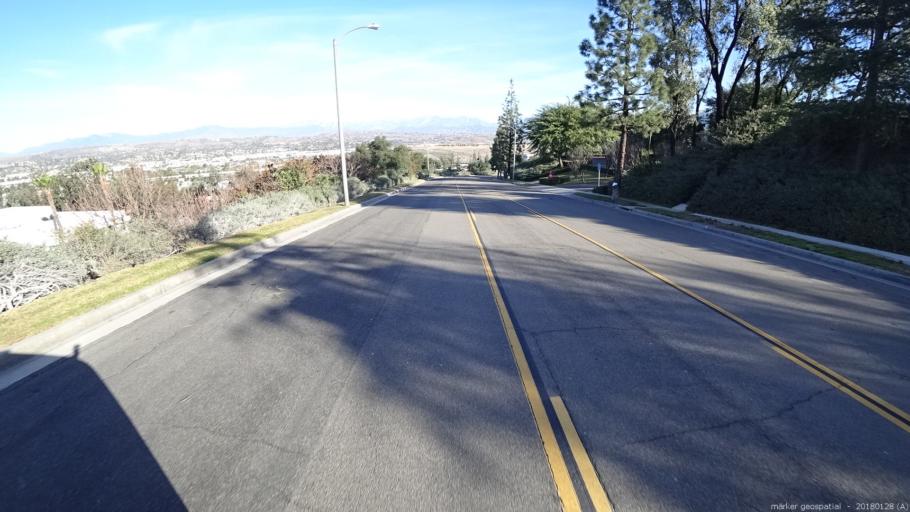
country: US
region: California
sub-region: Los Angeles County
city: Walnut
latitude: 33.9944
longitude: -117.8385
